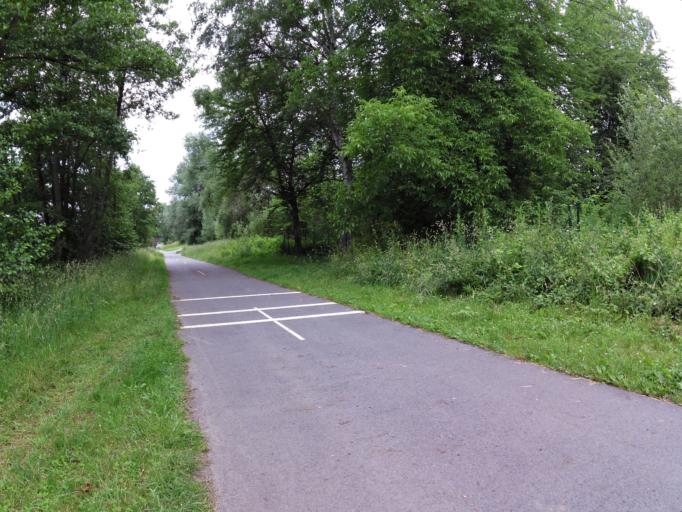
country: FR
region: Champagne-Ardenne
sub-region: Departement des Ardennes
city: Charleville-Mezieres
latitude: 49.7565
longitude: 4.7315
